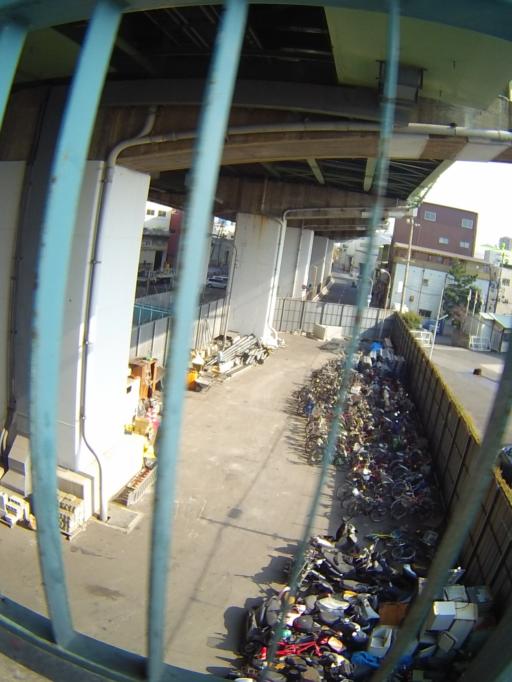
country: JP
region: Osaka
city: Osaka-shi
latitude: 34.6604
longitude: 135.4668
